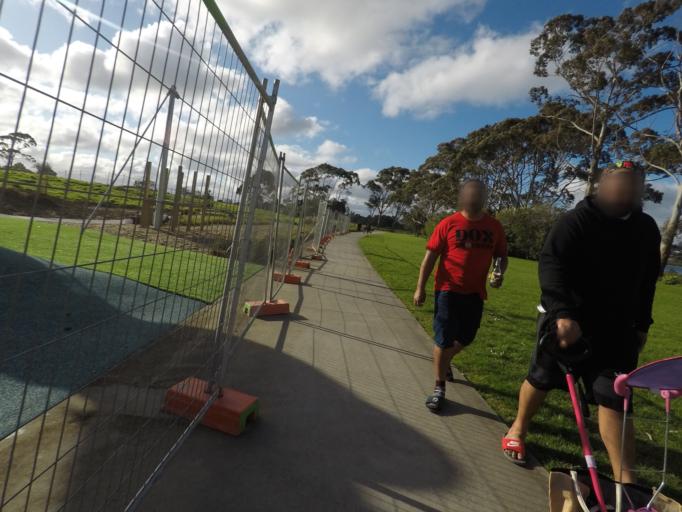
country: NZ
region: Auckland
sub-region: Auckland
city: Rosebank
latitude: -36.8939
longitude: 174.6714
